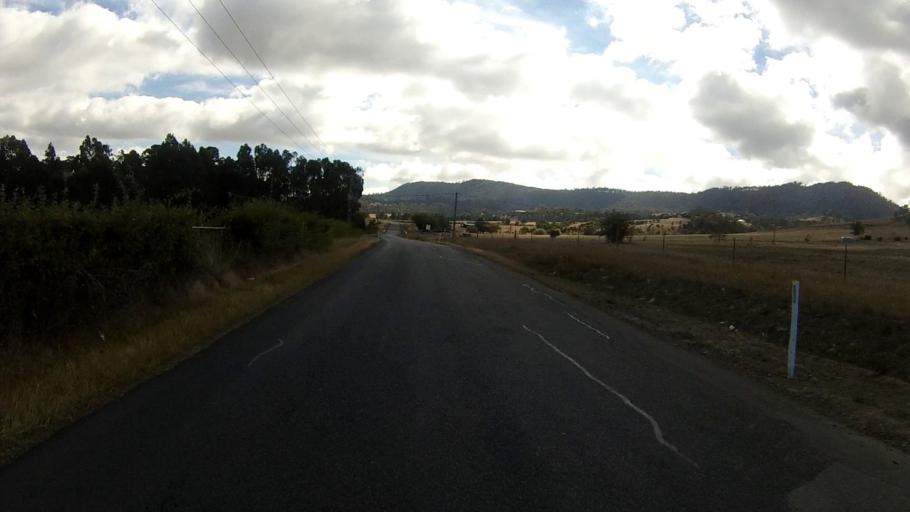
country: AU
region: Tasmania
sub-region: Brighton
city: Old Beach
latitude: -42.7689
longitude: 147.2956
